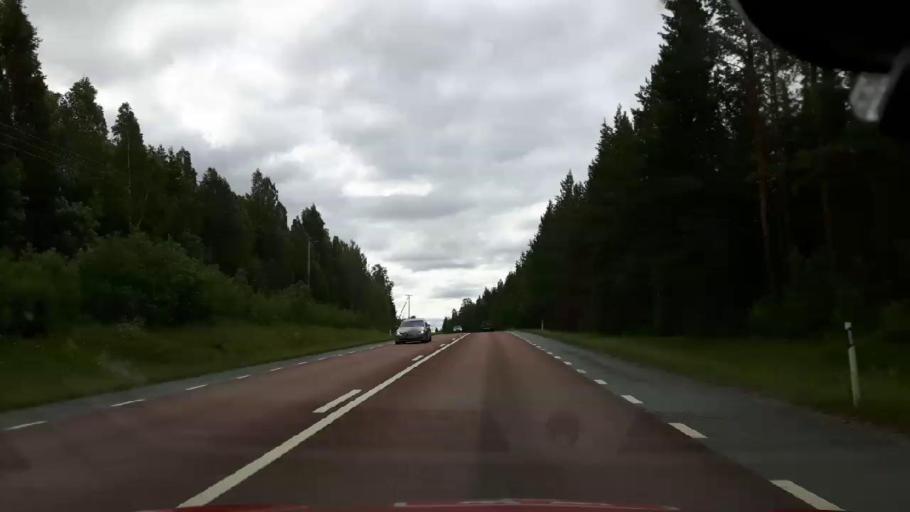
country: SE
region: Jaemtland
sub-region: Braecke Kommun
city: Braecke
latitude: 62.8012
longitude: 15.3707
